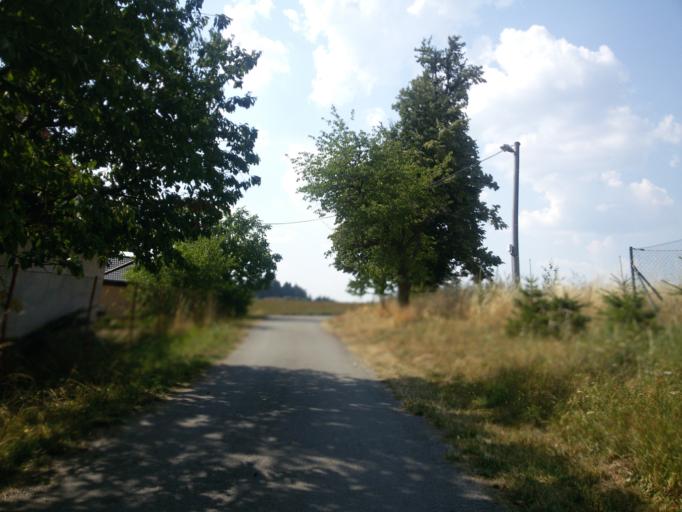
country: CZ
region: South Moravian
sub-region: Okres Brno-Venkov
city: Lomnice
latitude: 49.4461
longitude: 16.4601
